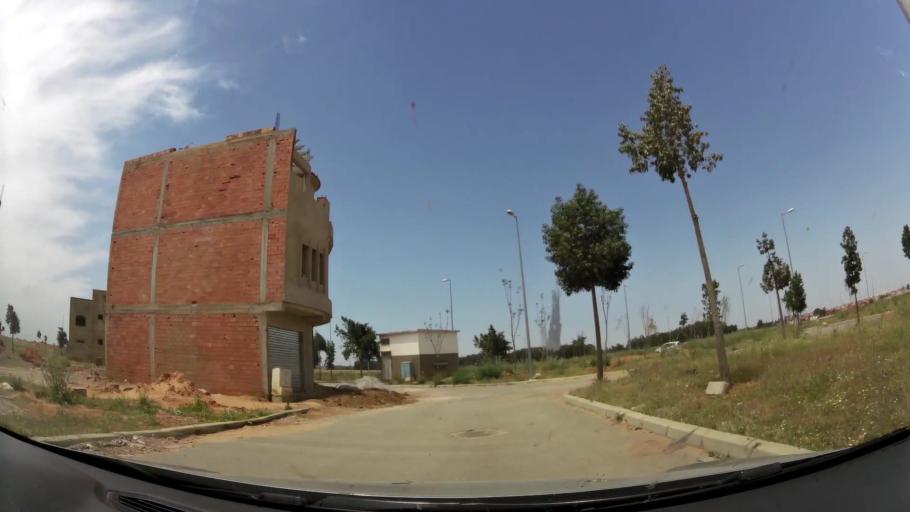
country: MA
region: Rabat-Sale-Zemmour-Zaer
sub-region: Khemisset
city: Khemisset
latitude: 33.8158
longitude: -6.0912
